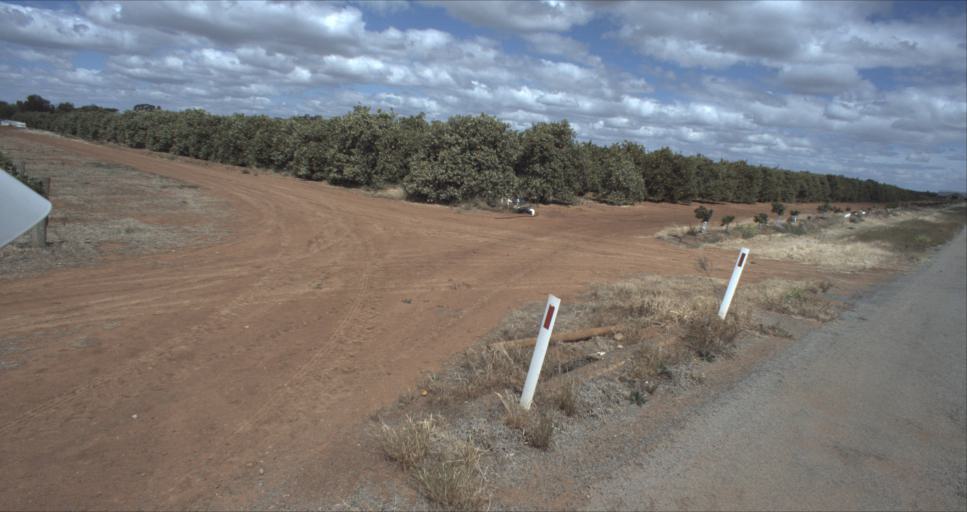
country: AU
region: New South Wales
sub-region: Leeton
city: Leeton
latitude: -34.5867
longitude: 146.3912
